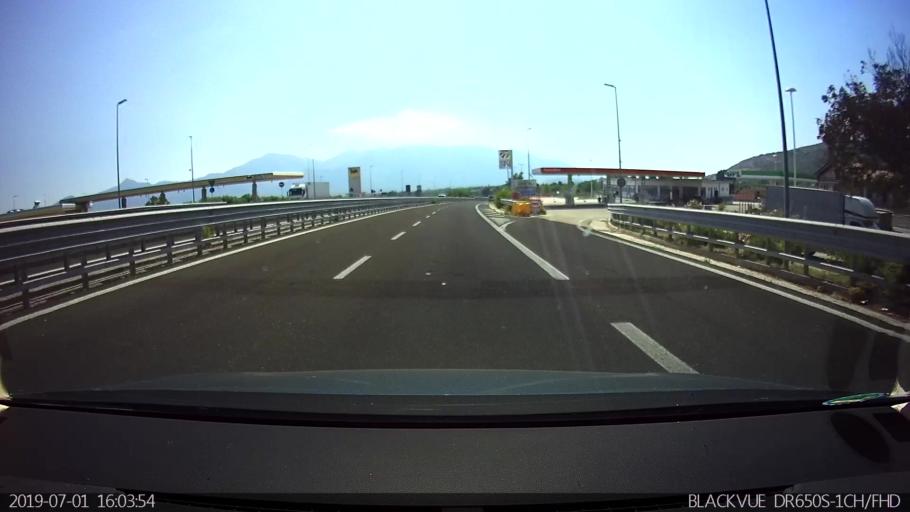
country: IT
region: Latium
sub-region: Provincia di Frosinone
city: Tecchiena
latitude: 41.6701
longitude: 13.3230
